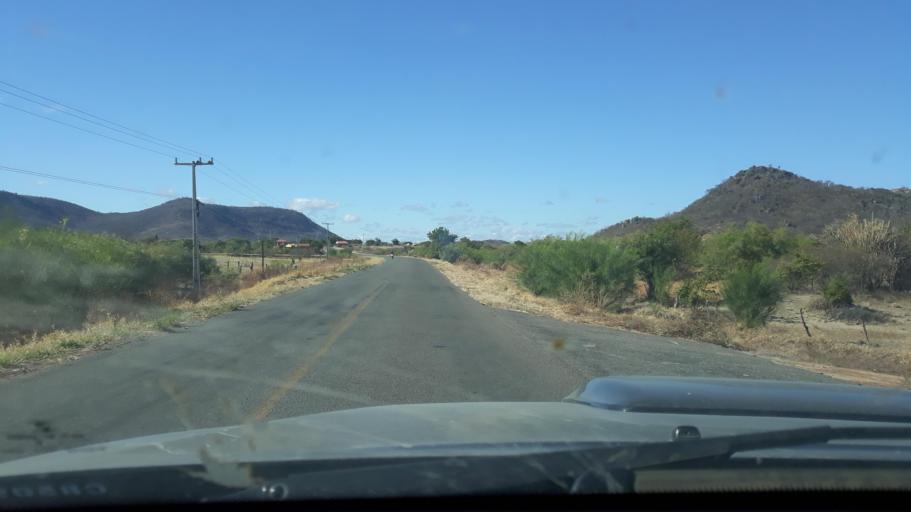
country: BR
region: Bahia
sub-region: Guanambi
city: Guanambi
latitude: -14.1086
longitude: -42.8657
